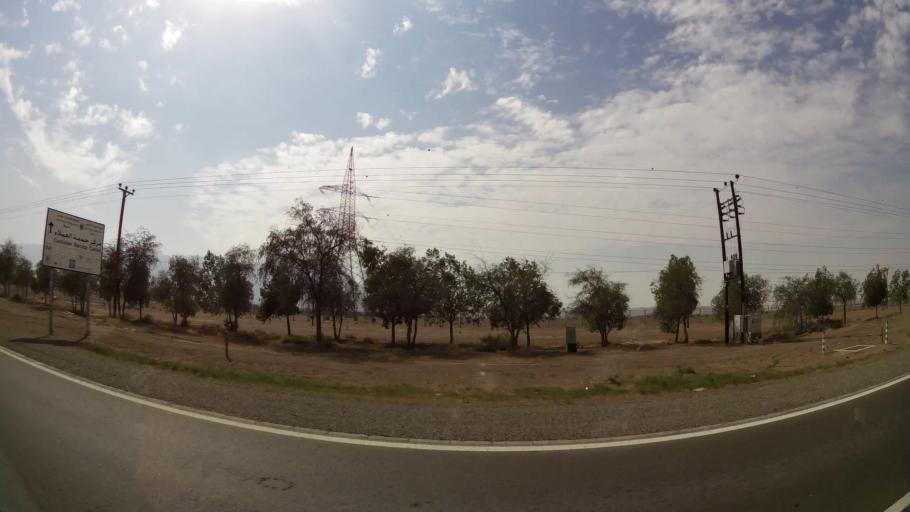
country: AE
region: Abu Dhabi
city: Al Ain
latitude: 24.1149
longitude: 55.8244
